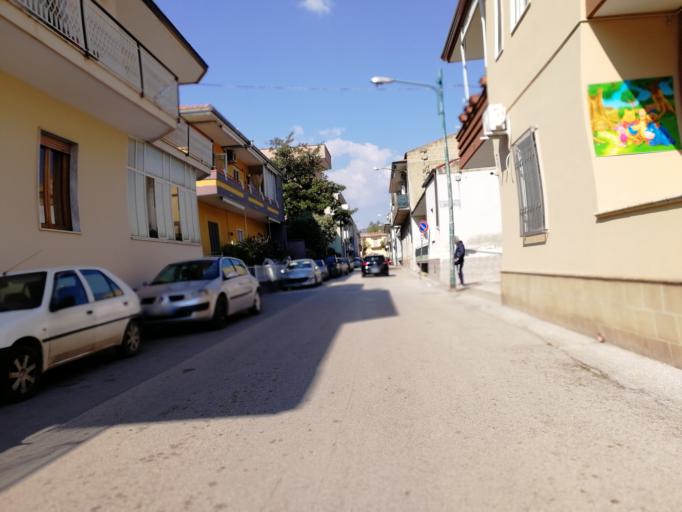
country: IT
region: Campania
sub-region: Provincia di Caserta
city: San Prisco
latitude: 41.0853
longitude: 14.2745
